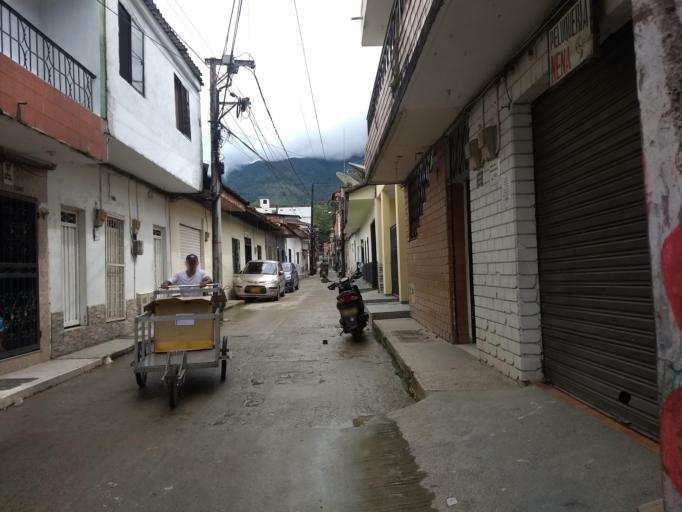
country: CO
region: Antioquia
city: San Carlos
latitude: 6.1871
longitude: -74.9927
